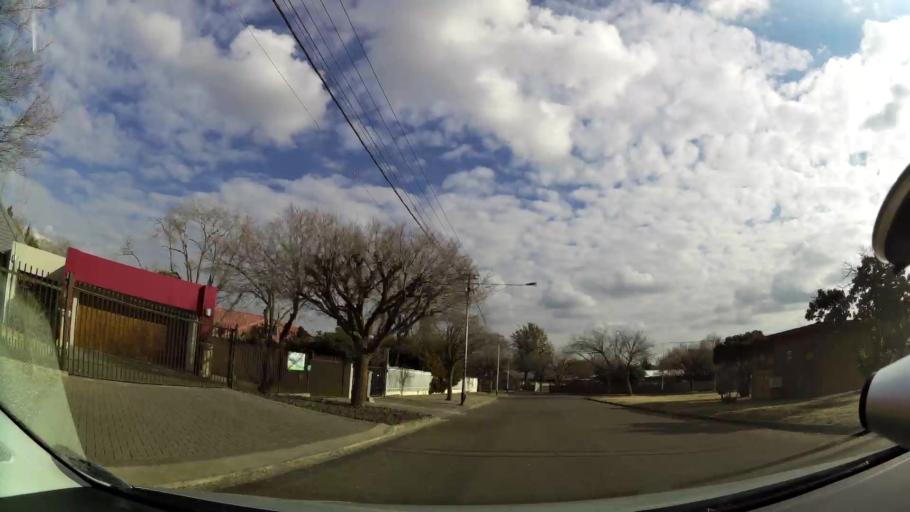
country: ZA
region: Orange Free State
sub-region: Mangaung Metropolitan Municipality
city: Bloemfontein
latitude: -29.0802
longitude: 26.2168
